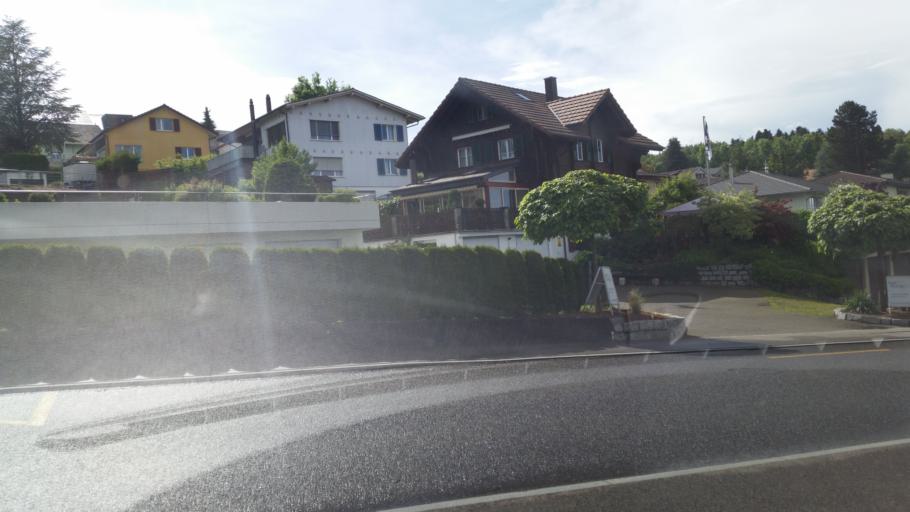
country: CH
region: Aargau
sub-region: Bezirk Bremgarten
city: Wohlen
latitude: 47.3315
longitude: 8.2741
